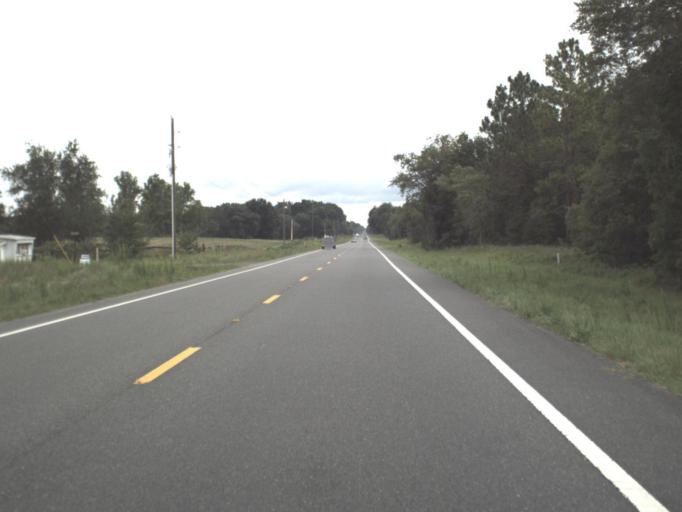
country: US
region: Florida
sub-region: Levy County
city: Williston Highlands
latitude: 29.2220
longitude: -82.4409
